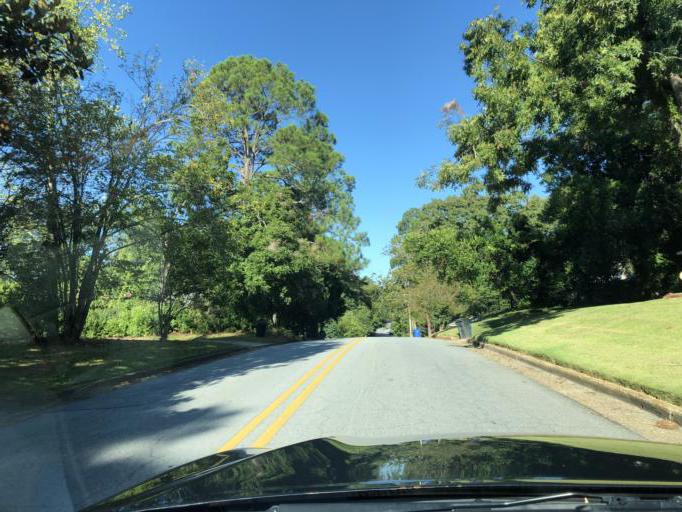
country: US
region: Georgia
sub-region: Muscogee County
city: Columbus
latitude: 32.4786
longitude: -84.9512
